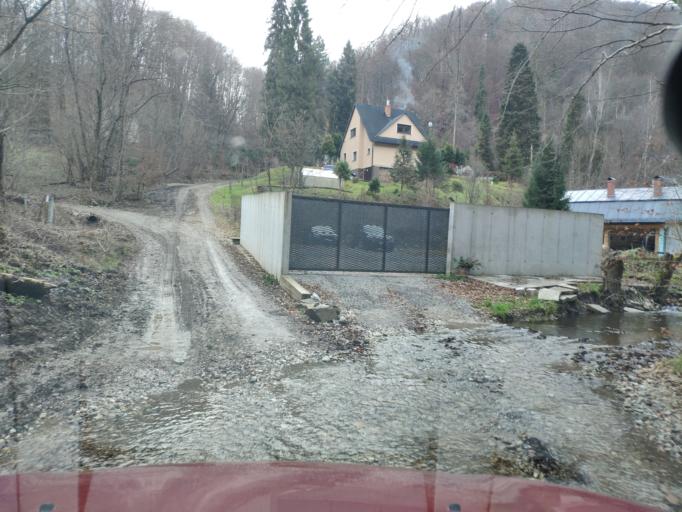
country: SK
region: Kosicky
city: Gelnica
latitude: 48.8175
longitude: 21.0560
